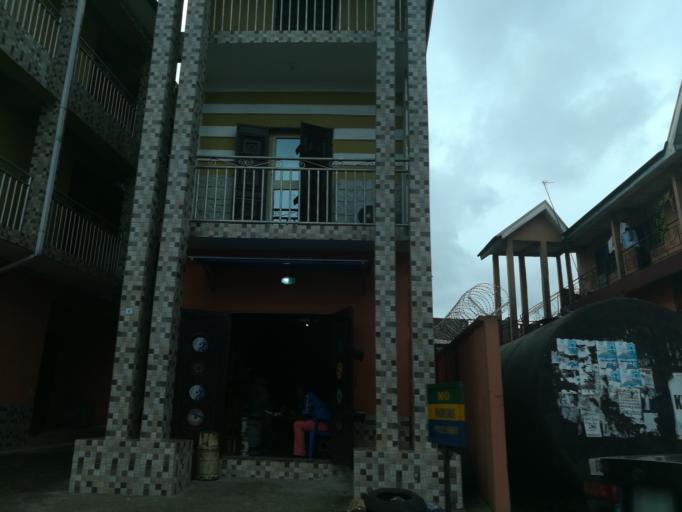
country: NG
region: Rivers
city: Port Harcourt
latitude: 4.8068
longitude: 6.9904
